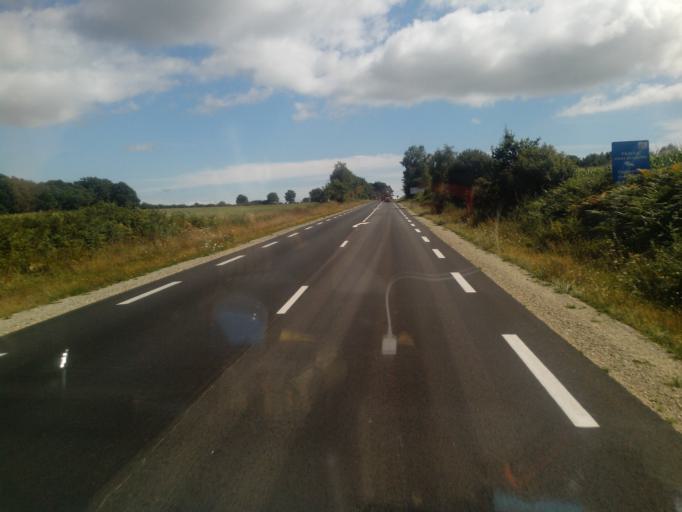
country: FR
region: Brittany
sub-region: Departement du Morbihan
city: Peaule
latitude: 47.5940
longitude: -2.3780
